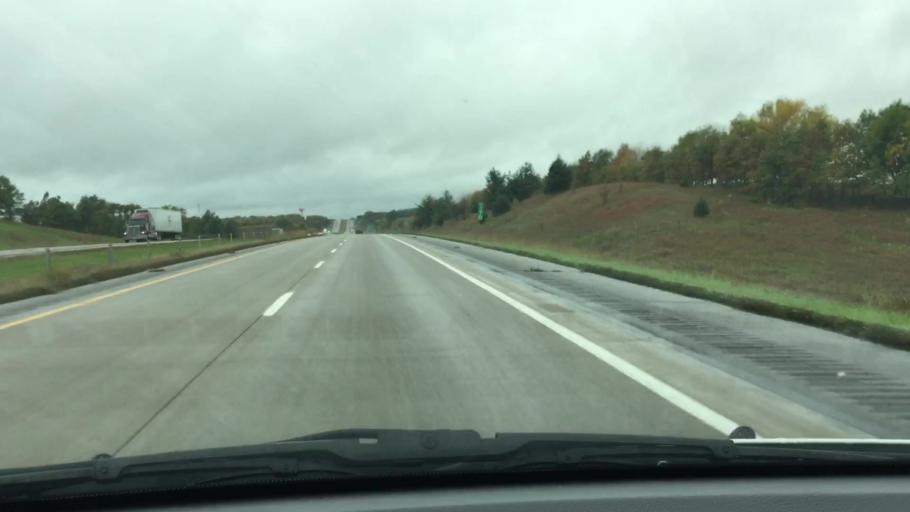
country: US
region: Iowa
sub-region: Jasper County
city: Newton
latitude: 41.6814
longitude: -92.9671
